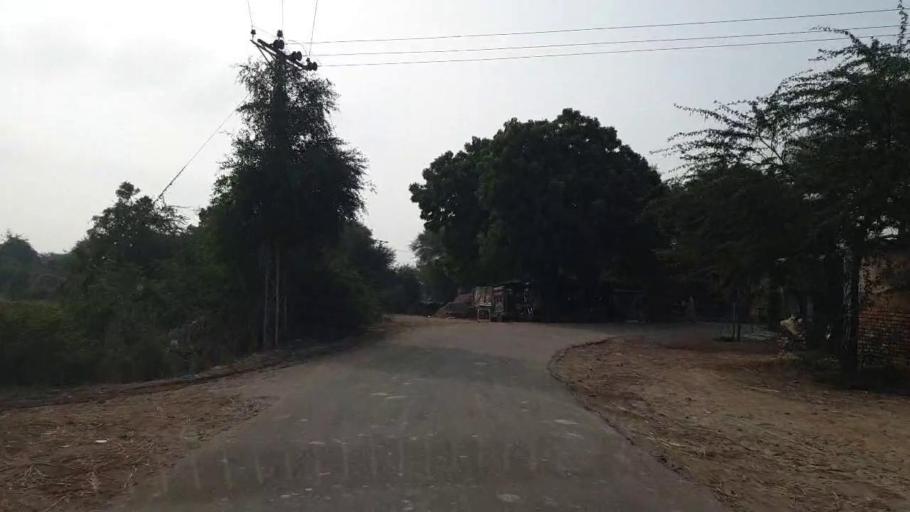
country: PK
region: Sindh
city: Matli
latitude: 24.9938
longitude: 68.6411
